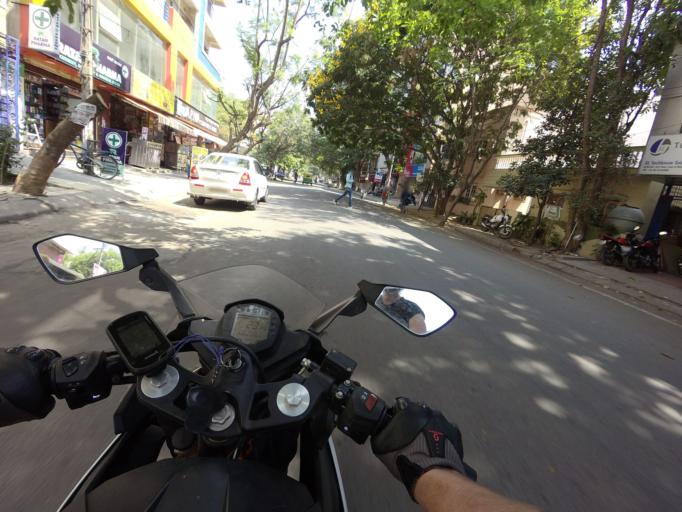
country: IN
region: Karnataka
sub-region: Bangalore Urban
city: Bangalore
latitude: 13.0029
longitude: 77.6610
